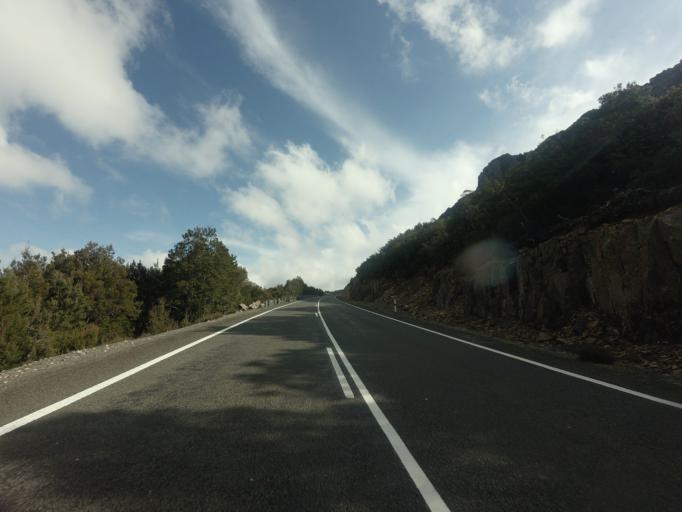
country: AU
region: Tasmania
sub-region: Meander Valley
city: Deloraine
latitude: -41.7294
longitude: 146.7204
